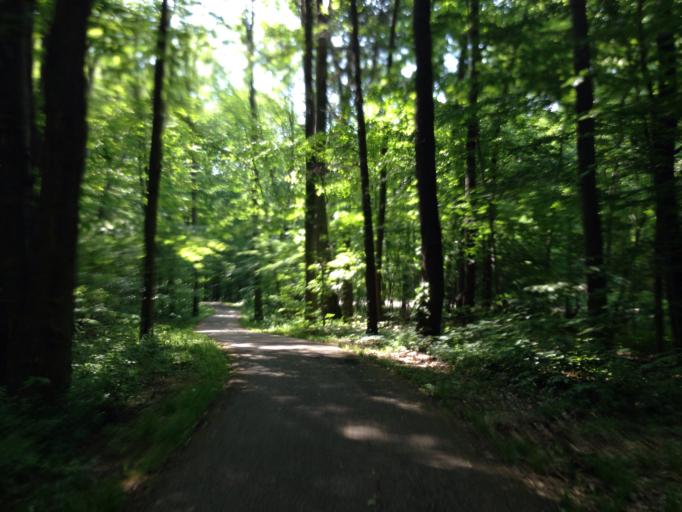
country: US
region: Ohio
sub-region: Cuyahoga County
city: Berea
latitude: 41.3911
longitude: -81.8707
